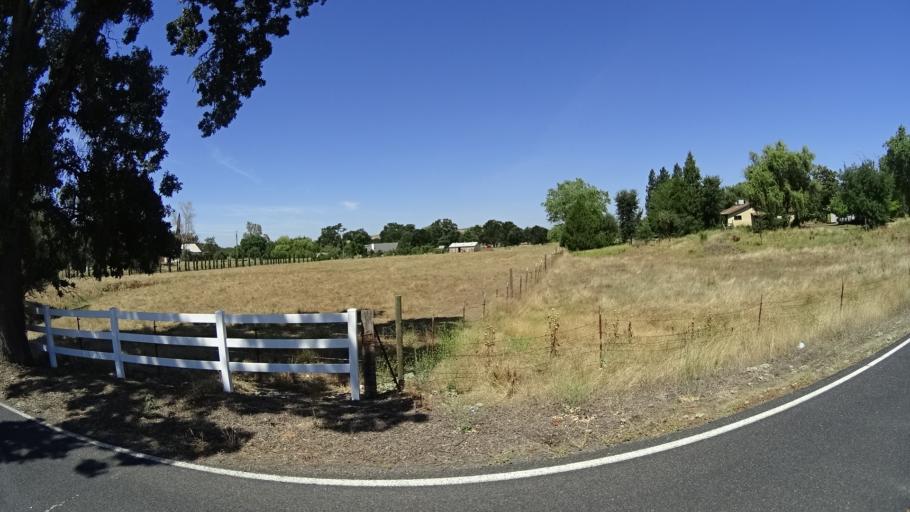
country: US
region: California
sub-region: Calaveras County
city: Rancho Calaveras
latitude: 38.1746
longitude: -120.9574
